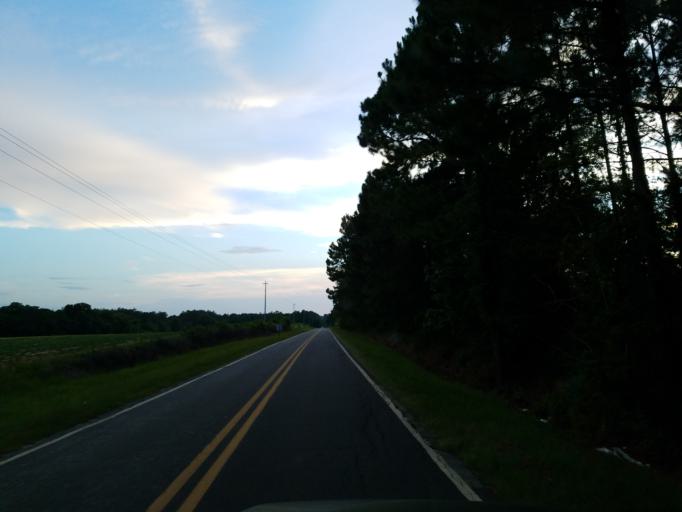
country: US
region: Georgia
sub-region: Crisp County
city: Cordele
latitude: 31.8377
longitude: -83.7533
